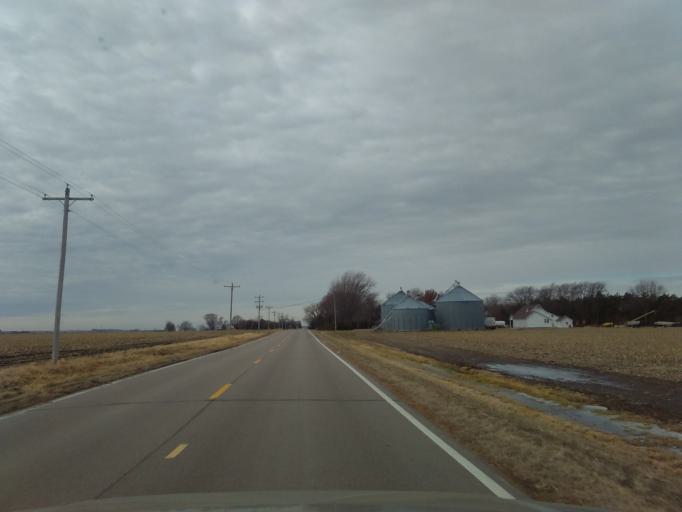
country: US
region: Nebraska
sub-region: Hall County
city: Grand Island
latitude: 40.7709
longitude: -98.4074
